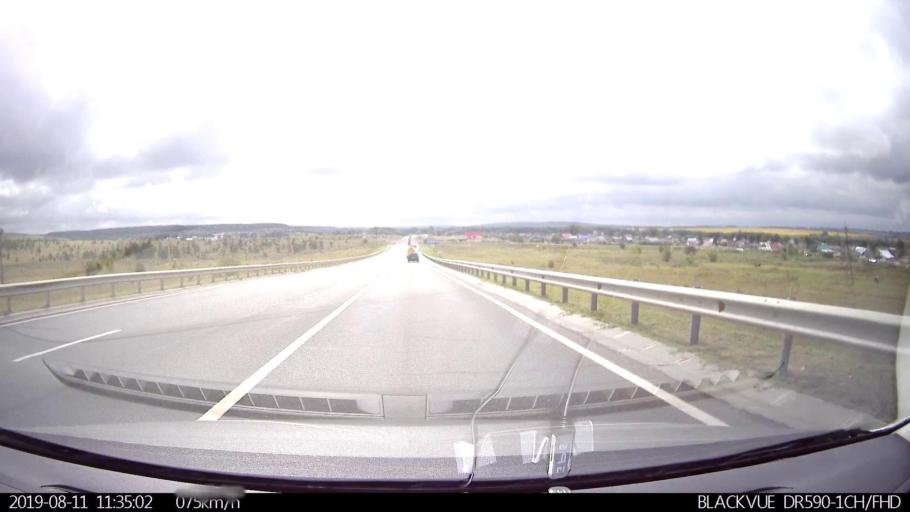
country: RU
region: Ulyanovsk
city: Silikatnyy
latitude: 54.0084
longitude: 48.2196
